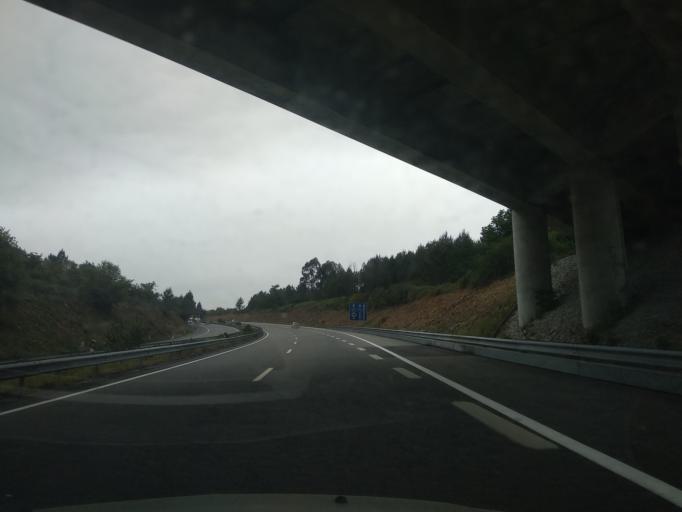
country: PT
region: Braga
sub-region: Barcelos
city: Barcelos
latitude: 41.5242
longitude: -8.5912
